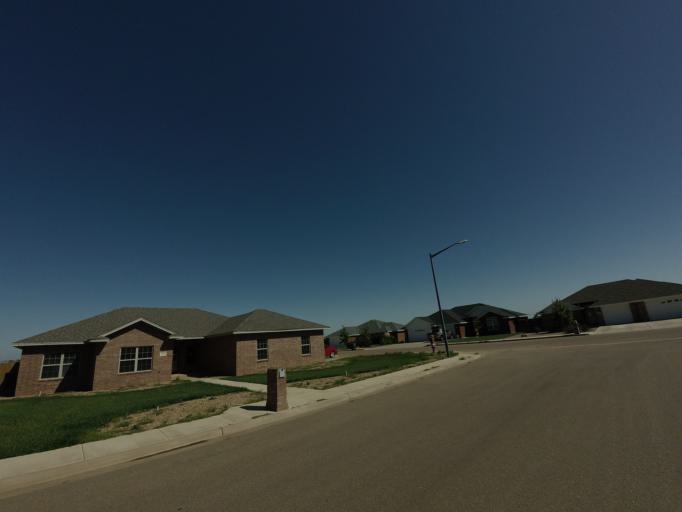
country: US
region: New Mexico
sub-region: Curry County
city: Clovis
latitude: 34.4227
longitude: -103.1573
